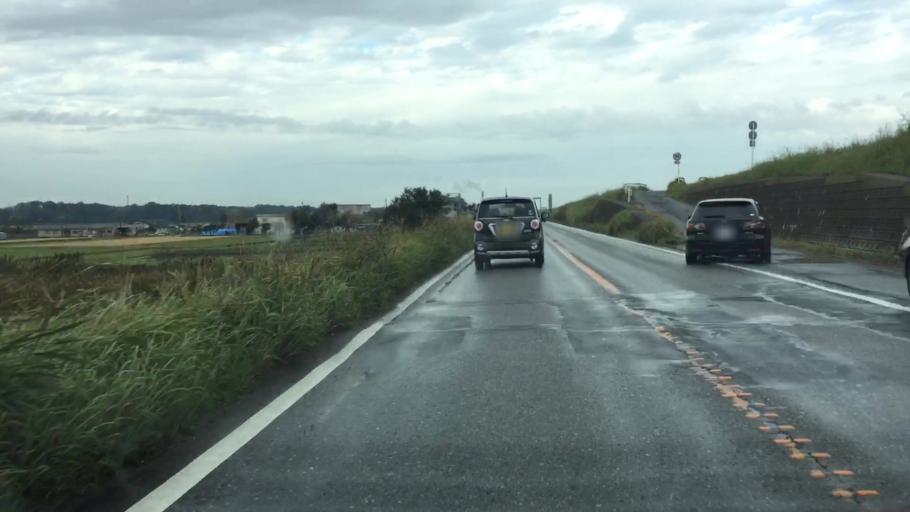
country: JP
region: Ibaraki
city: Toride
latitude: 35.8721
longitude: 140.1134
